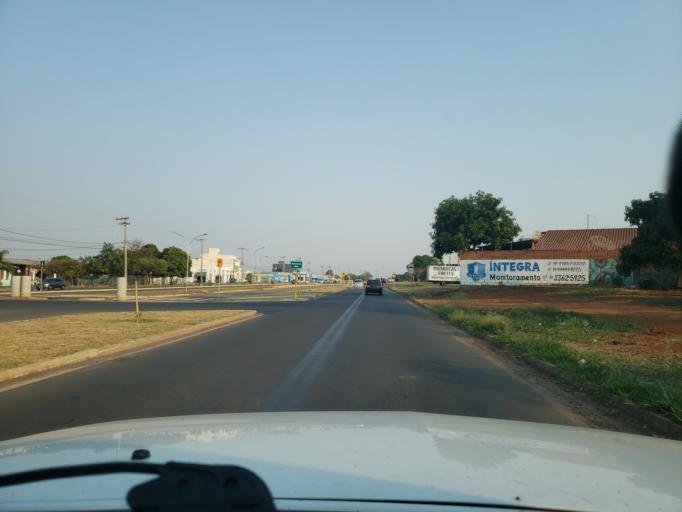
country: BR
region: Sao Paulo
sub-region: Moji-Guacu
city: Mogi-Gaucu
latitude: -22.3360
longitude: -46.9453
